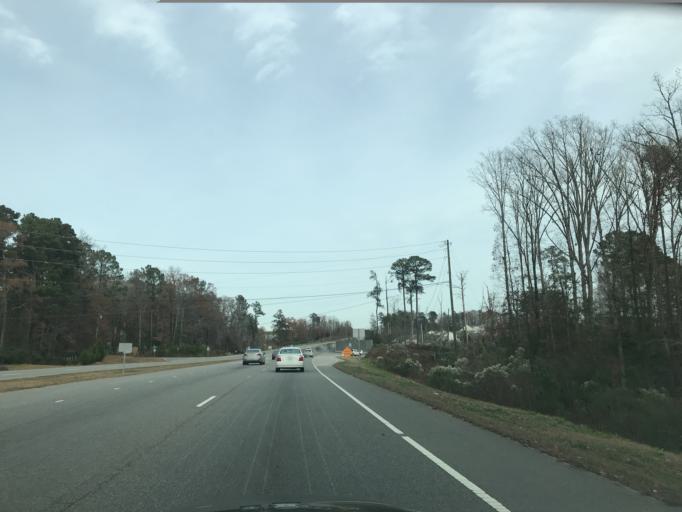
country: US
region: North Carolina
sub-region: Wake County
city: Rolesville
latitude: 35.8896
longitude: -78.5214
